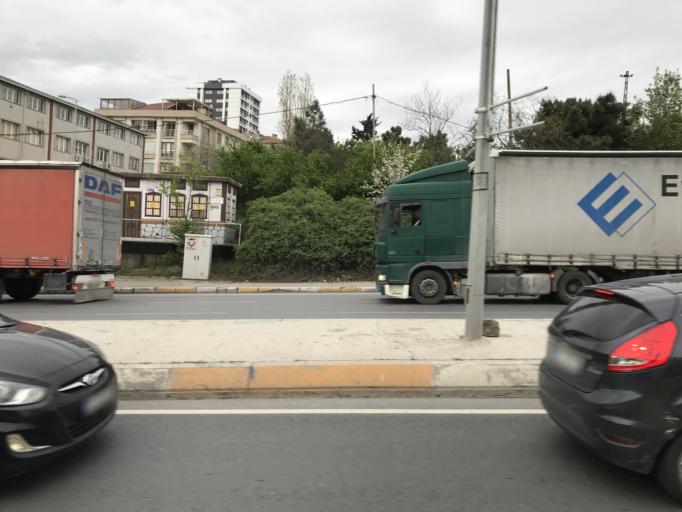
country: TR
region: Istanbul
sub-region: Atasehir
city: Atasehir
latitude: 40.9870
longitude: 29.1402
